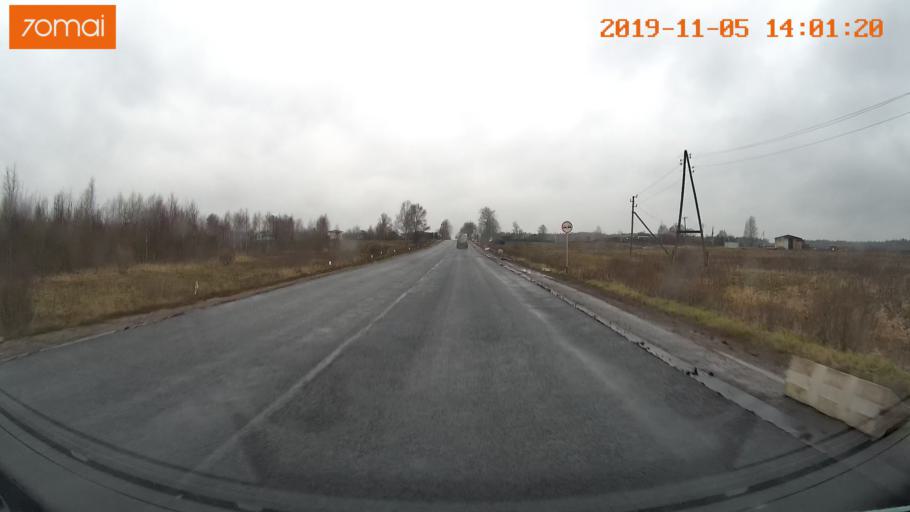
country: RU
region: Ivanovo
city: Kitovo
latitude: 57.0097
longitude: 41.2315
